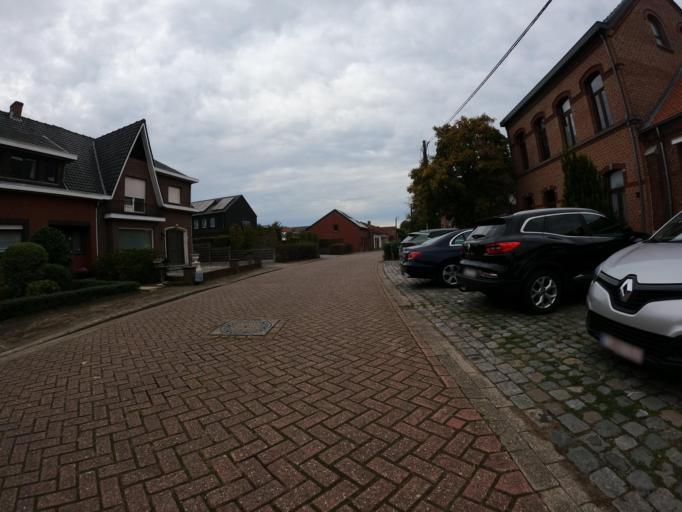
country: BE
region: Flanders
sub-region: Provincie Antwerpen
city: Herselt
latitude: 51.0893
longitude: 4.8729
